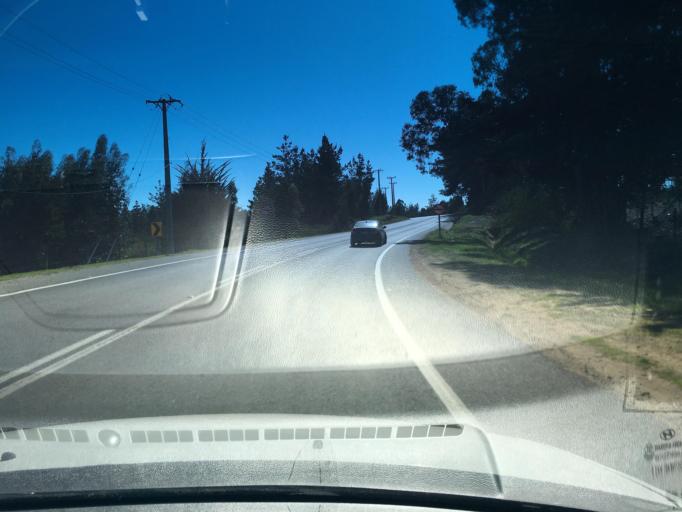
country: CL
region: Valparaiso
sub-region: San Antonio Province
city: El Tabo
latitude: -33.4245
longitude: -71.6736
